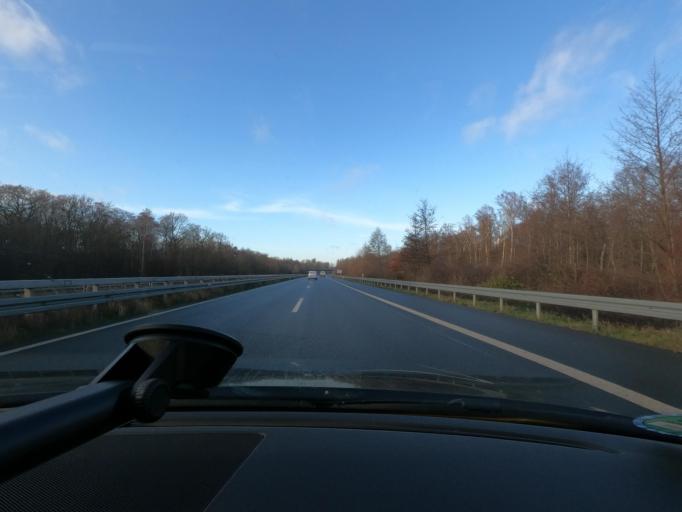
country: DE
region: North Rhine-Westphalia
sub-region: Regierungsbezirk Dusseldorf
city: Ratingen
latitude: 51.3503
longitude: 6.8118
